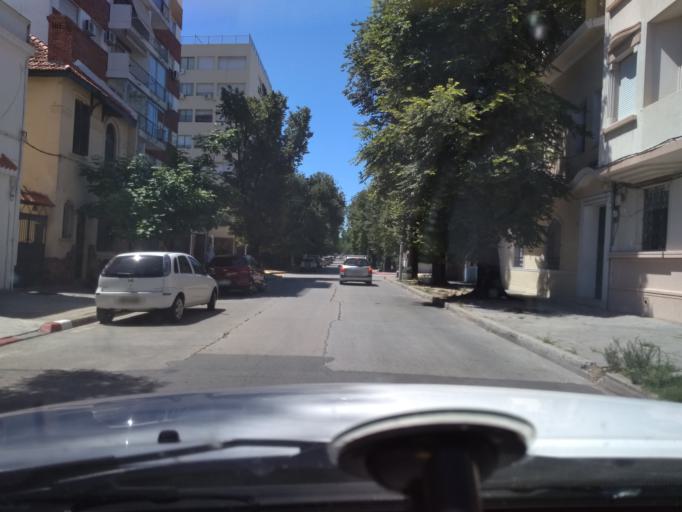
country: UY
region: Montevideo
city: Montevideo
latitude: -34.9069
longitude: -56.1517
